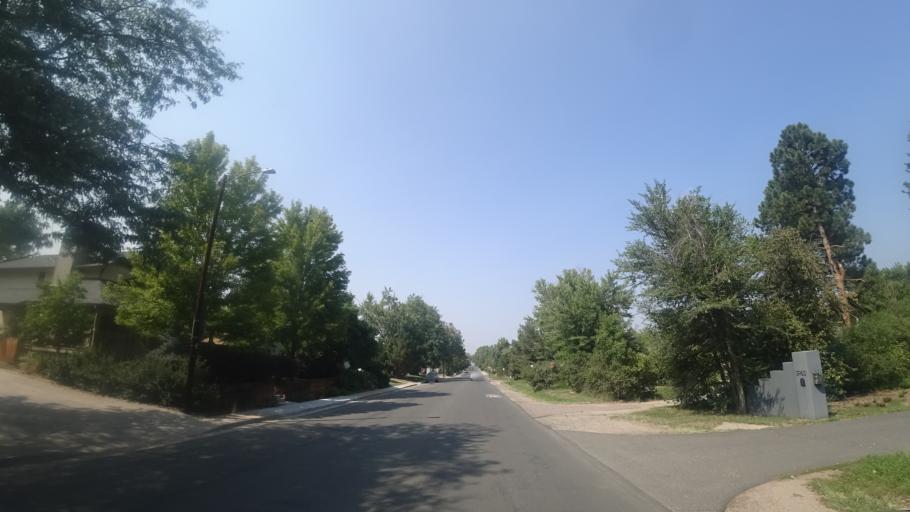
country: US
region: Colorado
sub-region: Arapahoe County
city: Englewood
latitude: 39.6447
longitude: -104.9784
